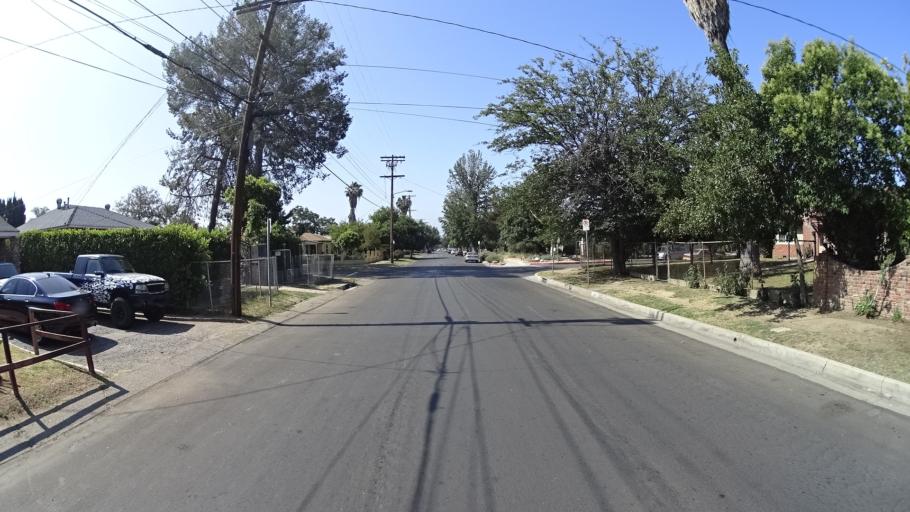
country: US
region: California
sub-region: Los Angeles County
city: Van Nuys
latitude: 34.1960
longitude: -118.4531
